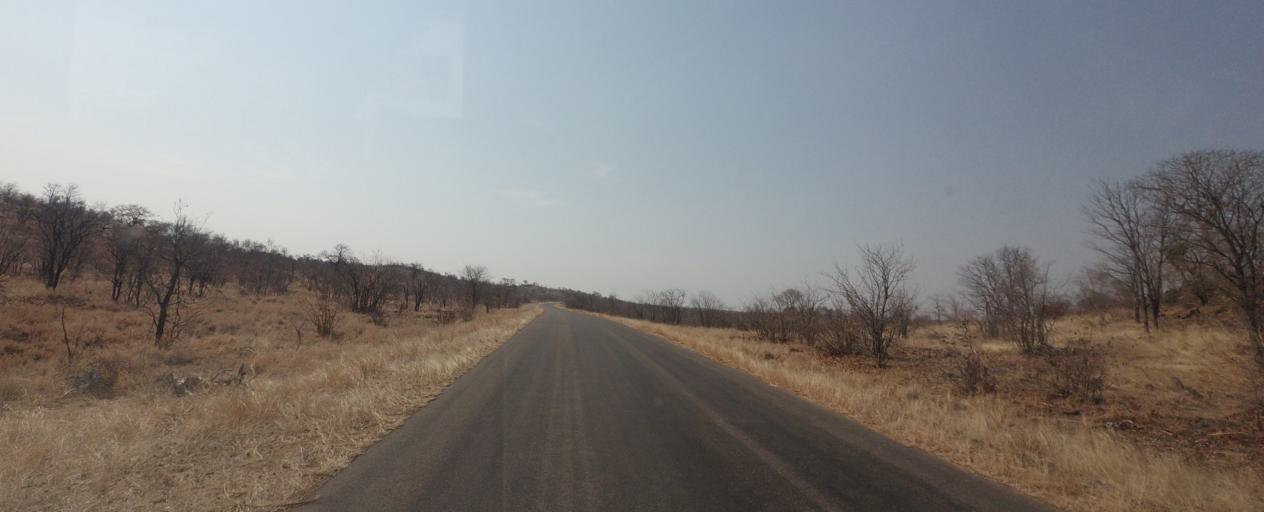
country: ZA
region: Limpopo
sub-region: Mopani District Municipality
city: Phalaborwa
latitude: -23.9935
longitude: 31.6431
